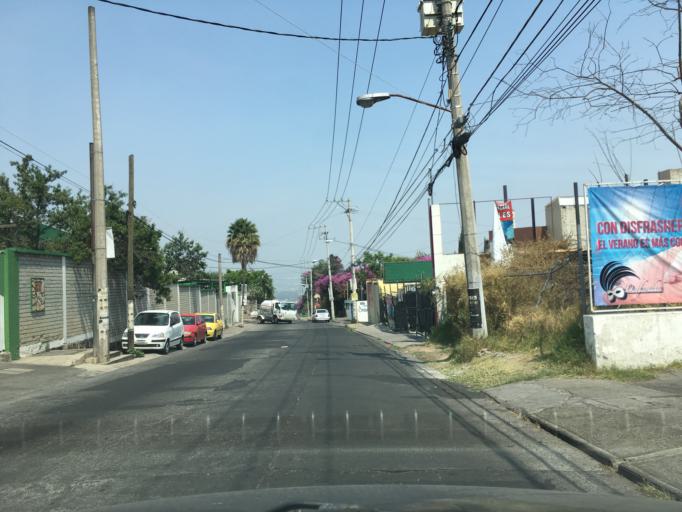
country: MX
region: Michoacan
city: Morelia
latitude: 19.6767
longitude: -101.1898
